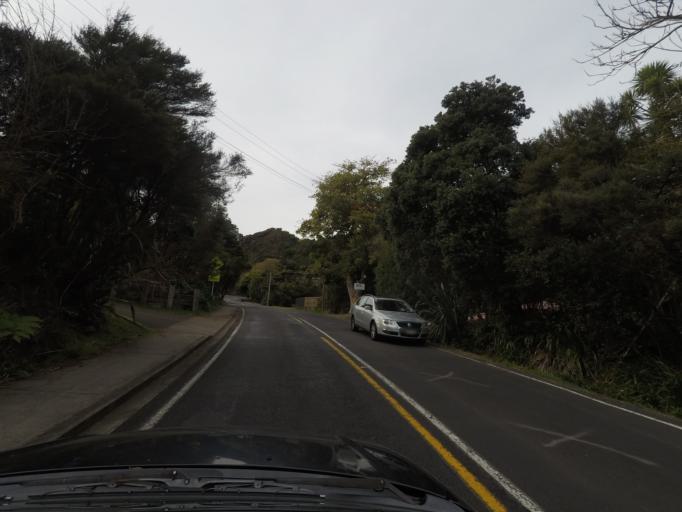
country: NZ
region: Auckland
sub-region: Auckland
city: Muriwai Beach
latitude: -36.9572
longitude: 174.4778
